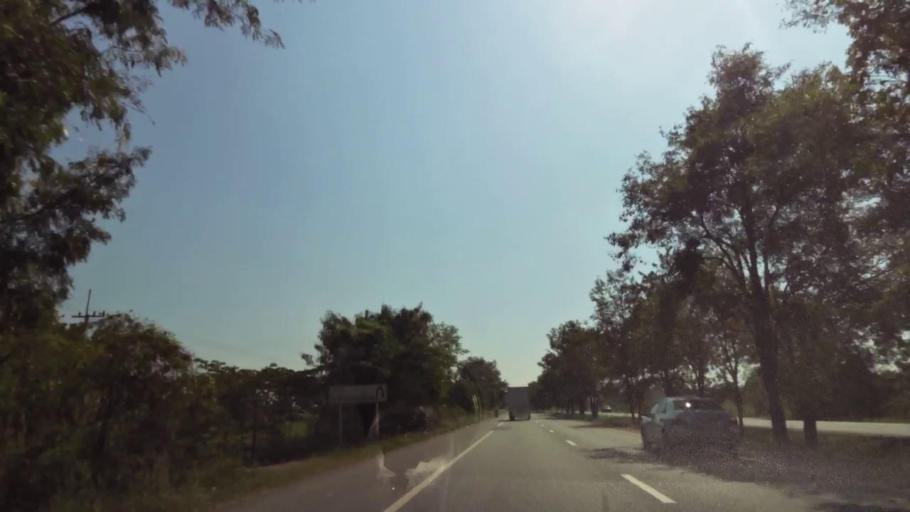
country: TH
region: Nakhon Sawan
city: Kao Liao
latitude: 15.9071
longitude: 100.1126
